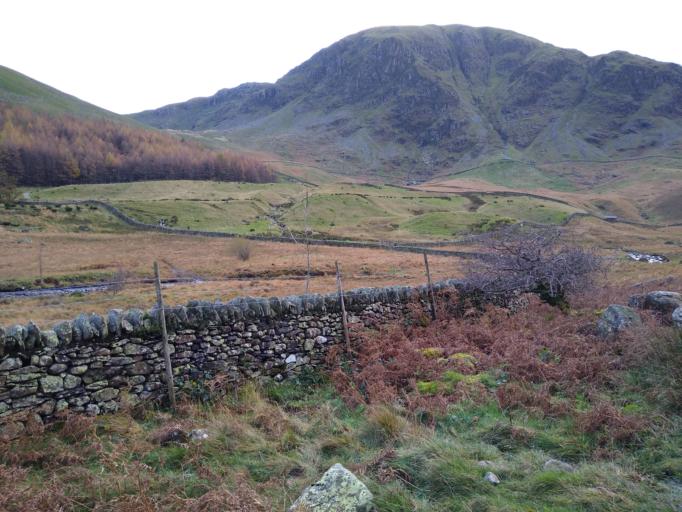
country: GB
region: England
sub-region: Cumbria
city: Windermere
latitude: 54.4906
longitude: -2.8231
